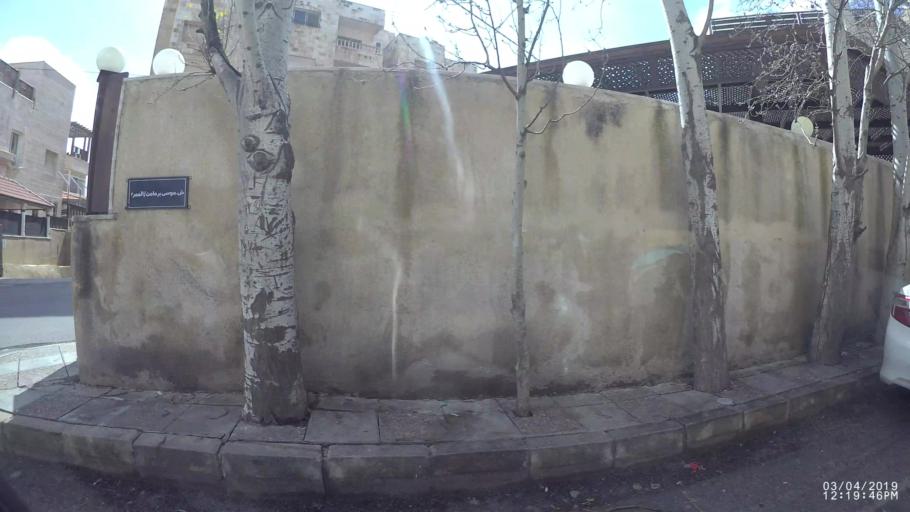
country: JO
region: Amman
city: Wadi as Sir
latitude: 31.9692
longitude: 35.8386
